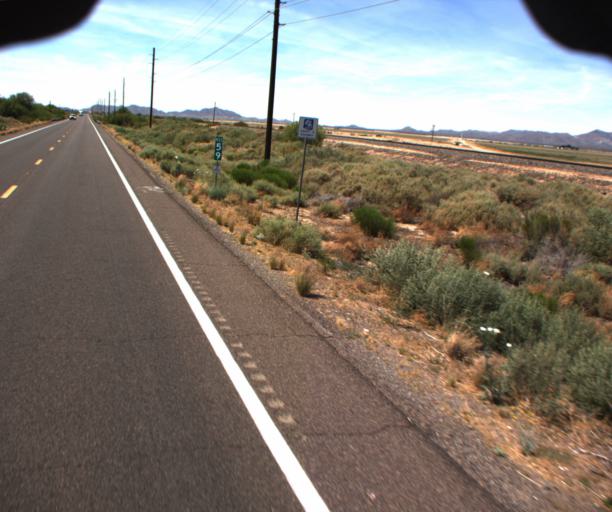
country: US
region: Arizona
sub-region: La Paz County
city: Salome
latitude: 33.8026
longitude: -113.5771
